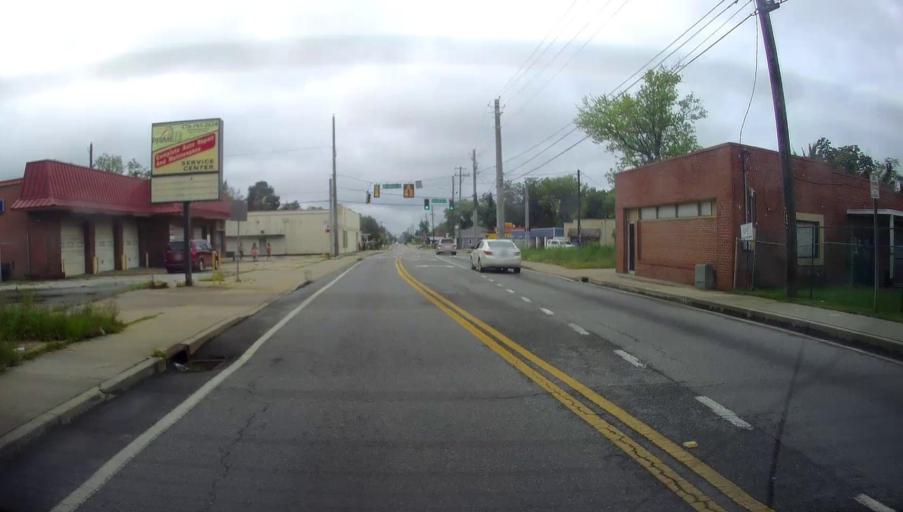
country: US
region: Georgia
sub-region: Bibb County
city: Macon
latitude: 32.8125
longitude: -83.6454
